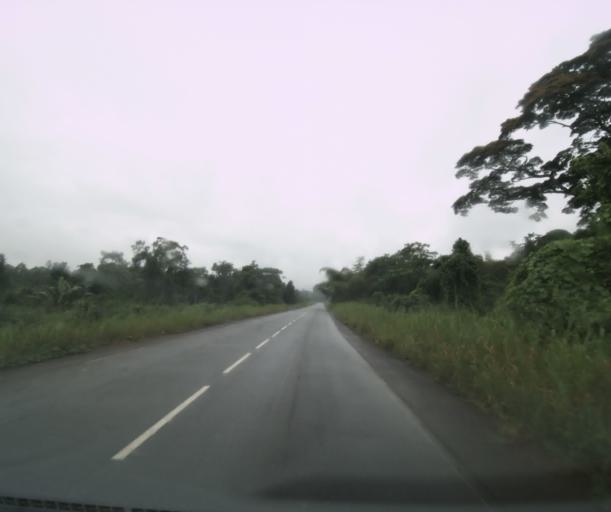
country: CM
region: Littoral
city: Edea
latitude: 3.4684
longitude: 10.1330
